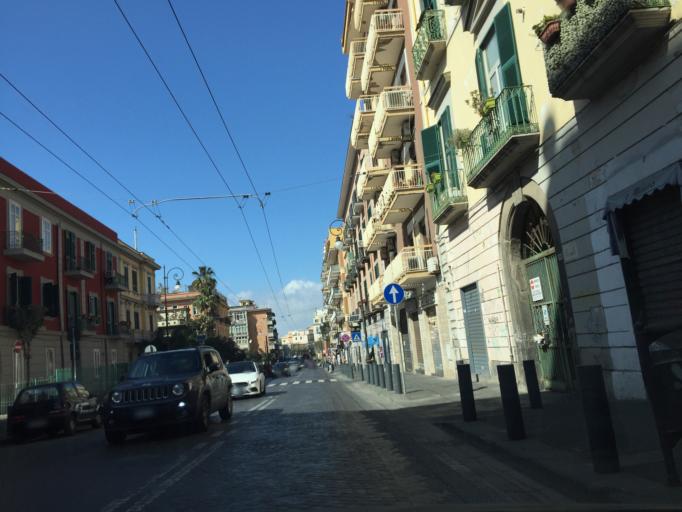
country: IT
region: Campania
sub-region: Provincia di Napoli
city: Portici
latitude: 40.8171
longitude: 14.3324
